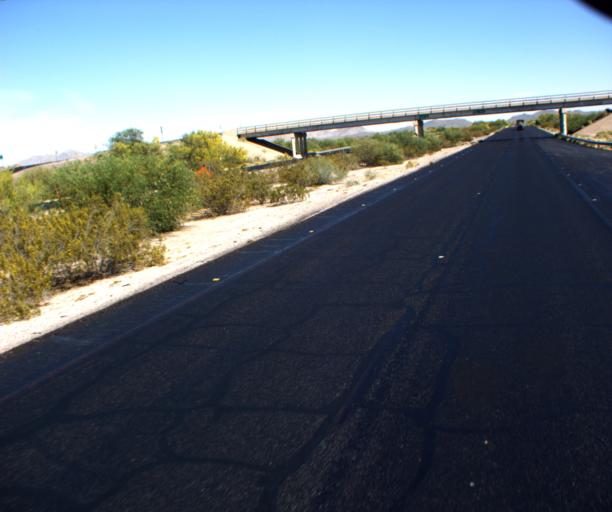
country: US
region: Arizona
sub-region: Pinal County
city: Maricopa
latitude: 32.8421
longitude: -112.2565
